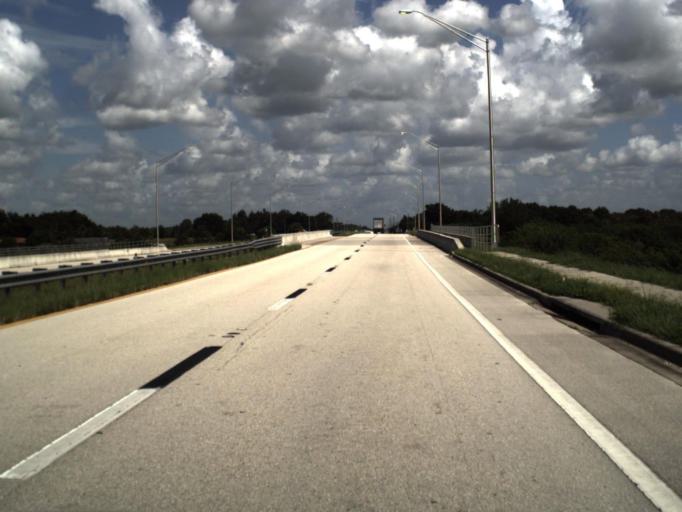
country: US
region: Florida
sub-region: Charlotte County
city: Cleveland
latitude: 26.9803
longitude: -81.9591
